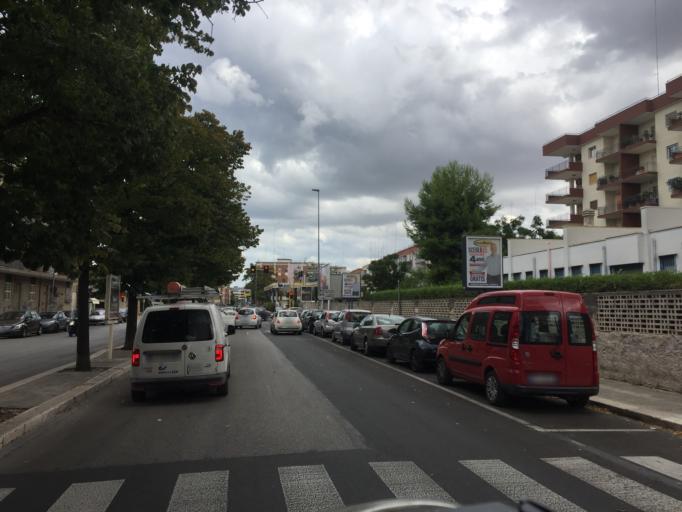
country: IT
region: Apulia
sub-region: Provincia di Bari
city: Bari
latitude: 41.1009
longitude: 16.8662
